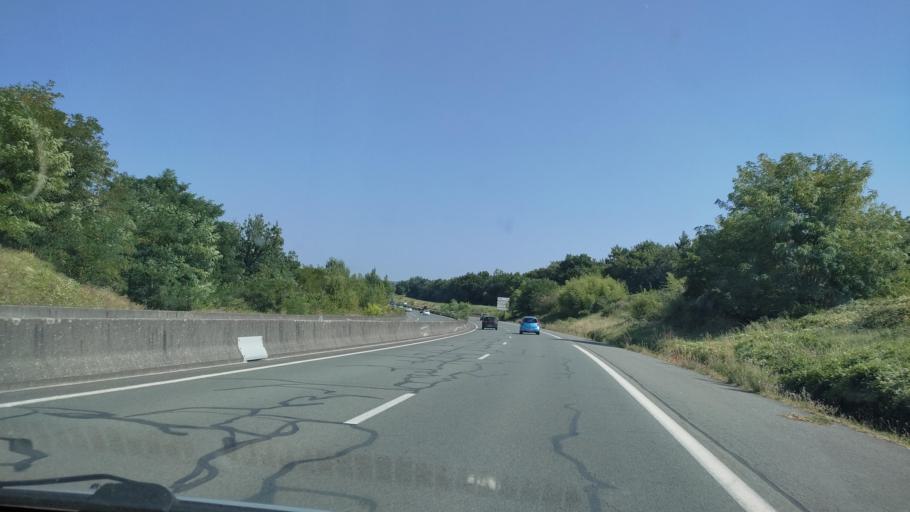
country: FR
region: Poitou-Charentes
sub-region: Departement de la Charente
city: Saint-Yrieix-sur-Charente
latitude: 45.6840
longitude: 0.1162
